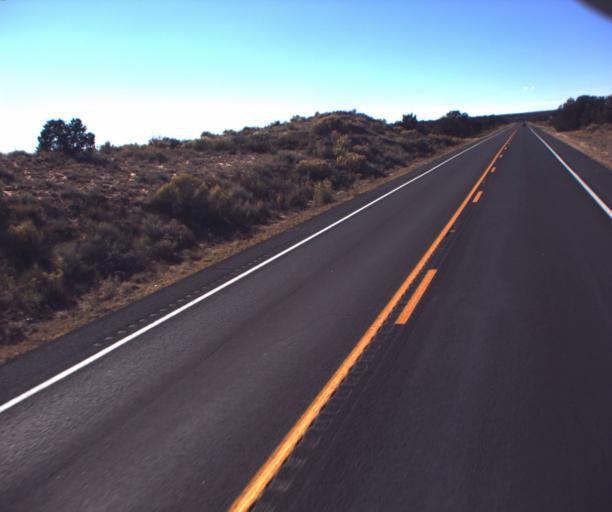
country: US
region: Arizona
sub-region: Coconino County
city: Kaibito
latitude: 36.5830
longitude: -110.8084
